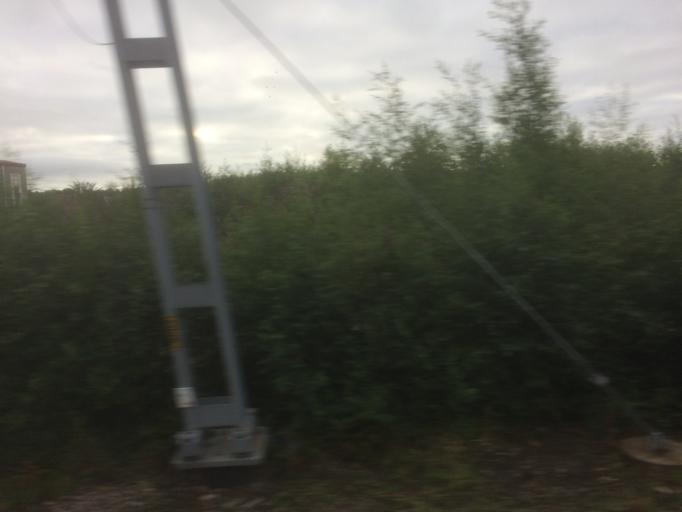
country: GB
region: Scotland
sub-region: Glasgow City
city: Glasgow
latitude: 55.8845
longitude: -4.2391
